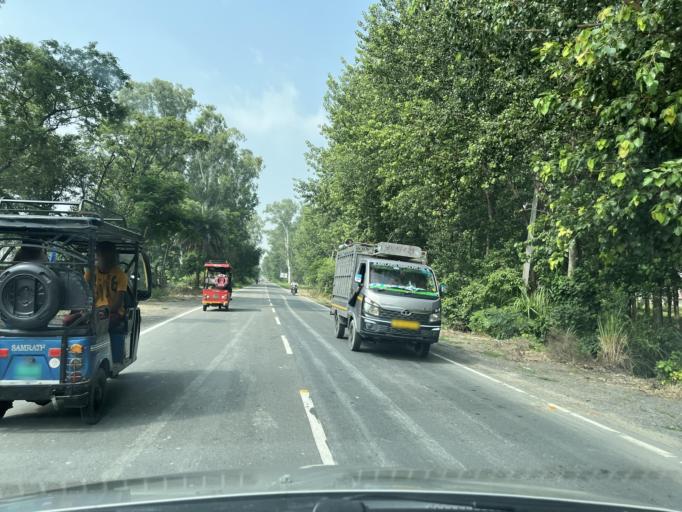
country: IN
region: Uttarakhand
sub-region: Udham Singh Nagar
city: Bazpur
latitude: 29.1766
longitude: 79.1734
